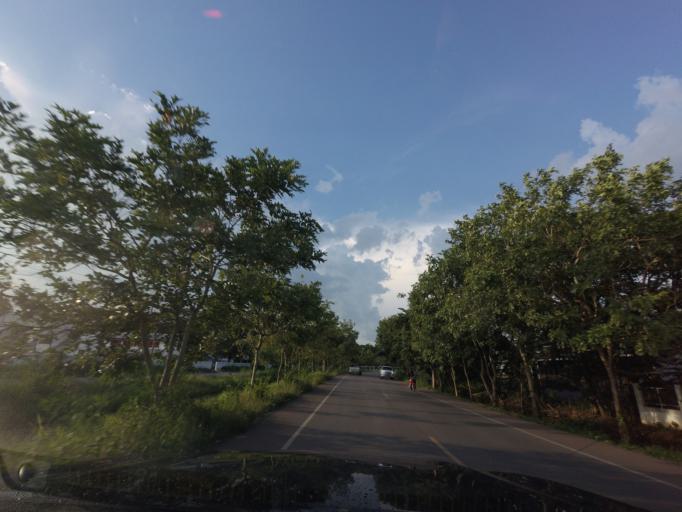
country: TH
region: Khon Kaen
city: Khon Kaen
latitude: 16.4200
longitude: 102.8602
